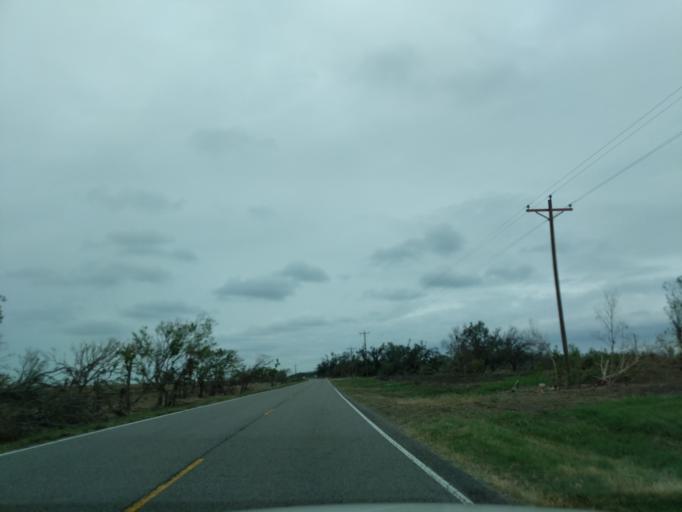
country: US
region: Louisiana
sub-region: Cameron Parish
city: Cameron
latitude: 29.7864
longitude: -93.1745
